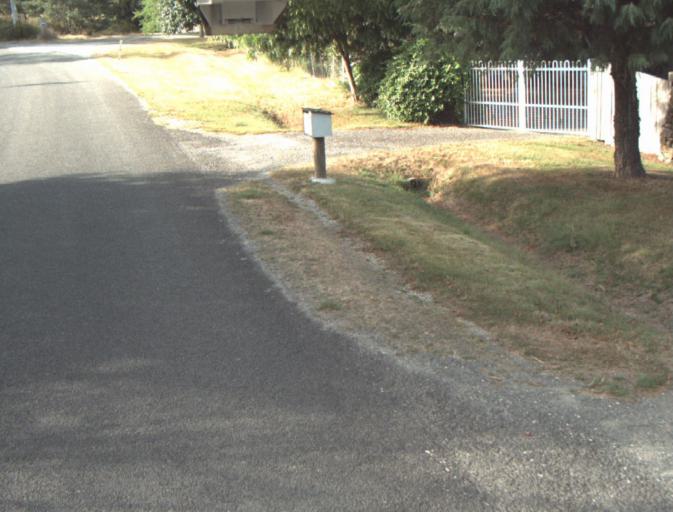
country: AU
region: Tasmania
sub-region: Launceston
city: Mayfield
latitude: -41.2697
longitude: 147.1675
